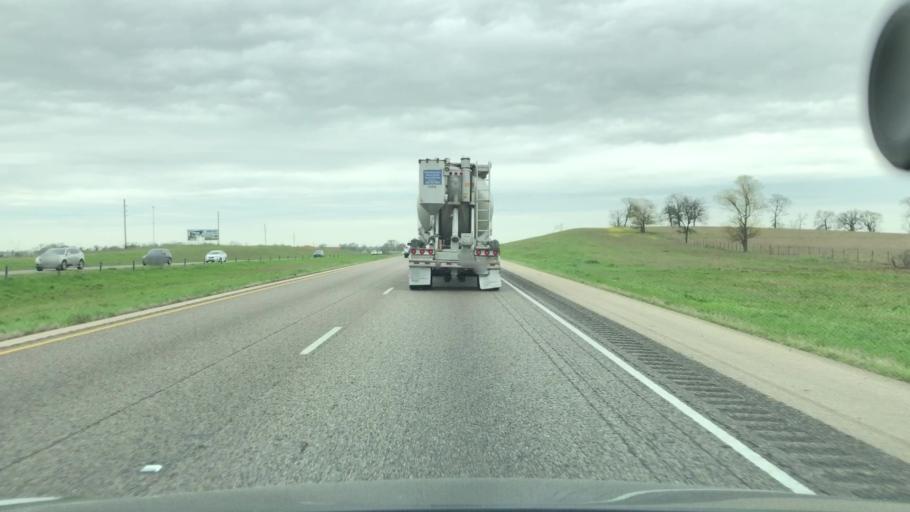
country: US
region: Texas
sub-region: Madison County
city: Madisonville
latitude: 31.0356
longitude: -95.9388
